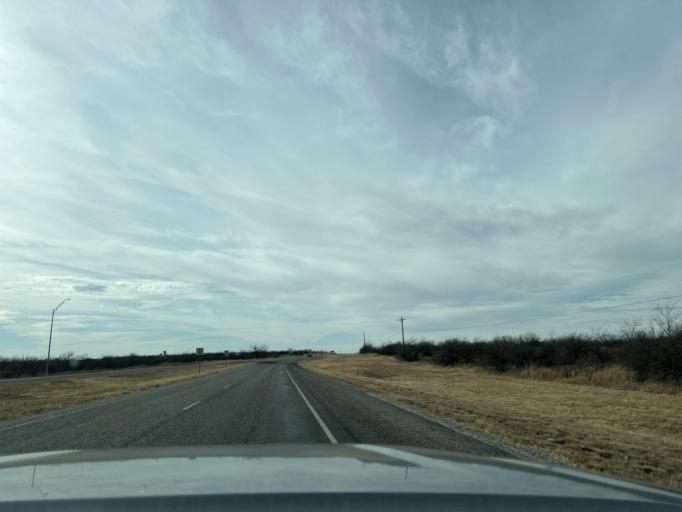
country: US
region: Texas
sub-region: Shackelford County
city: Albany
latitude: 32.7077
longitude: -99.4268
